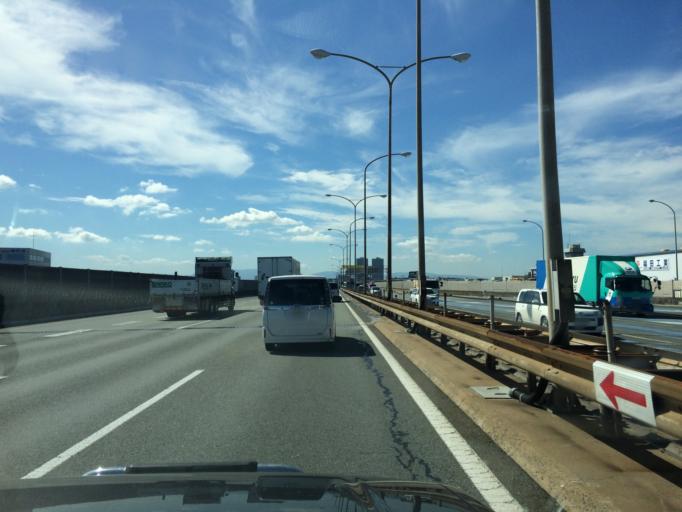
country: JP
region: Osaka
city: Yao
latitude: 34.6469
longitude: 135.5959
